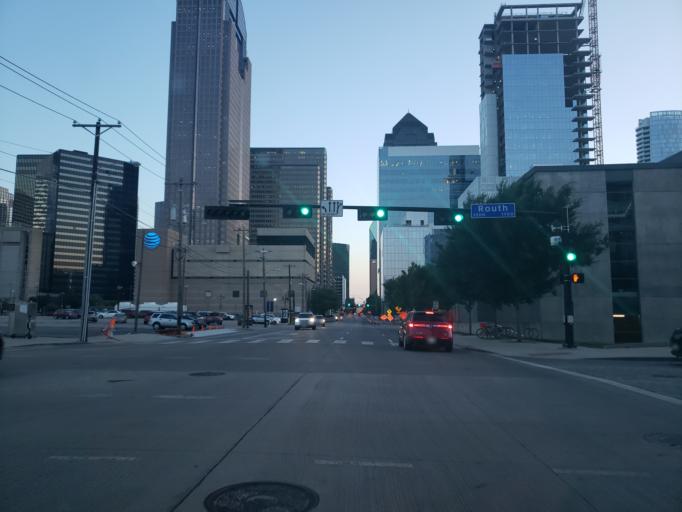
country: US
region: Texas
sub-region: Dallas County
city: Dallas
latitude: 32.7908
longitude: -96.7947
